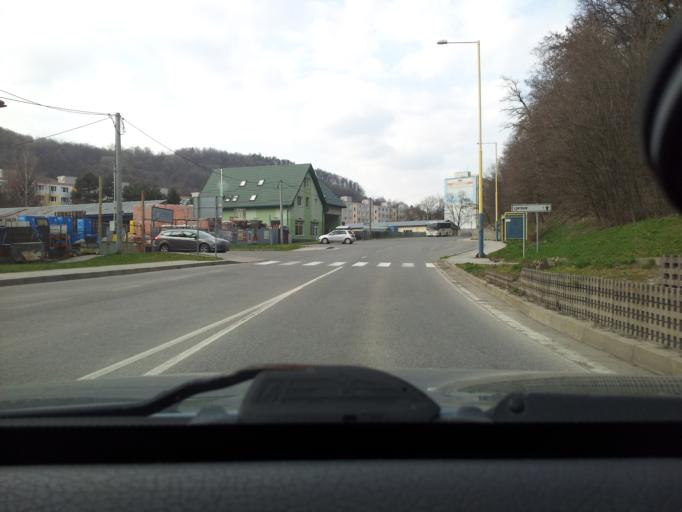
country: SK
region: Banskobystricky
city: Nova Bana
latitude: 48.4130
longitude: 18.6448
